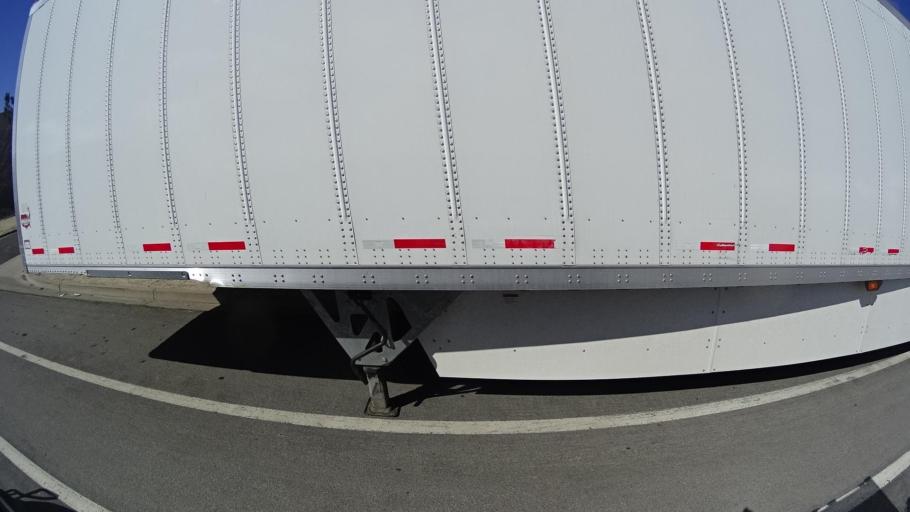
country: US
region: Nevada
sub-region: Washoe County
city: Lemmon Valley
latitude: 39.6519
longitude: -119.8970
